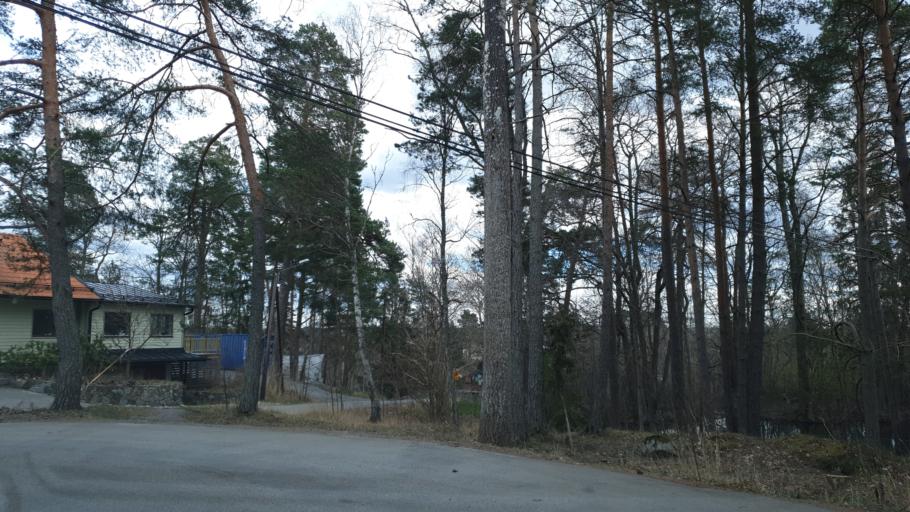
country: SE
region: Stockholm
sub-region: Nacka Kommun
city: Boo
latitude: 59.3219
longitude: 18.3052
